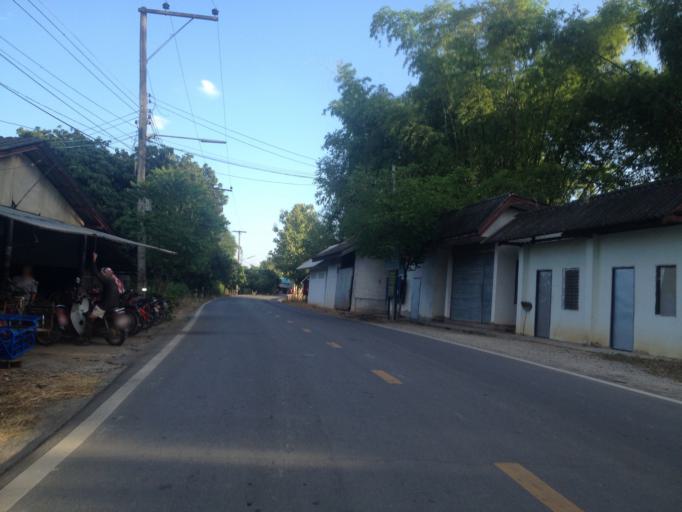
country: TH
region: Chiang Mai
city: San Pa Tong
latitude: 18.6040
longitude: 98.8586
